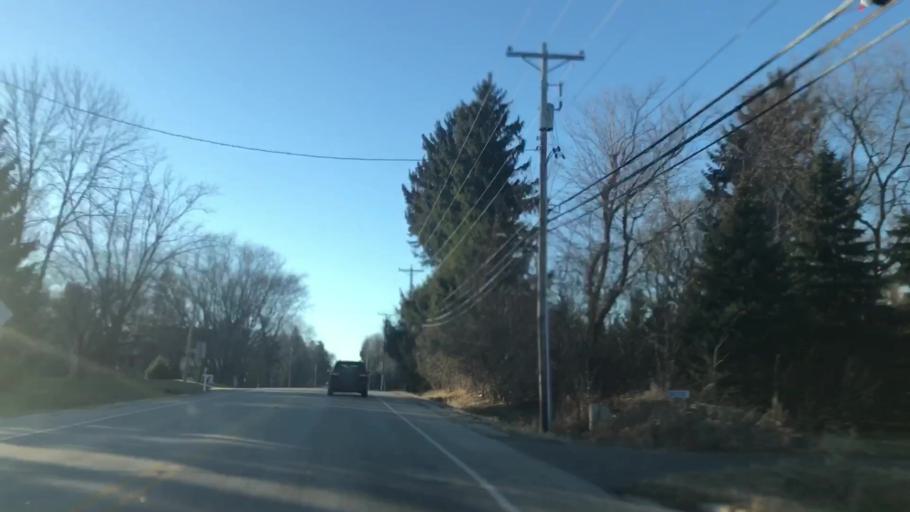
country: US
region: Wisconsin
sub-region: Ozaukee County
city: Cedarburg
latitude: 43.2935
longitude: -88.0065
